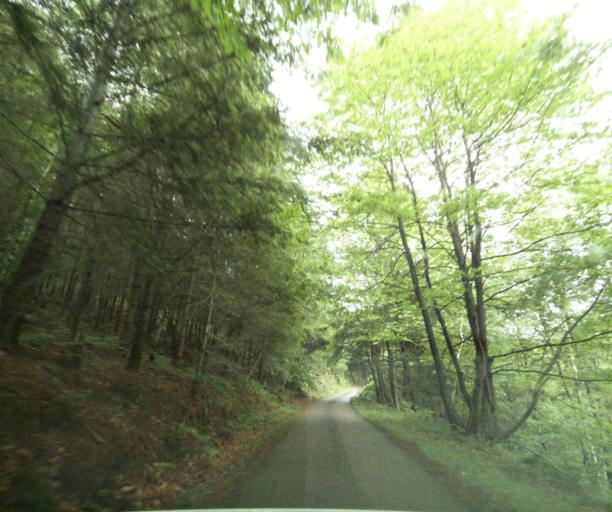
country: FR
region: Bourgogne
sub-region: Departement de Saone-et-Loire
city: Matour
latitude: 46.4464
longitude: 4.4676
